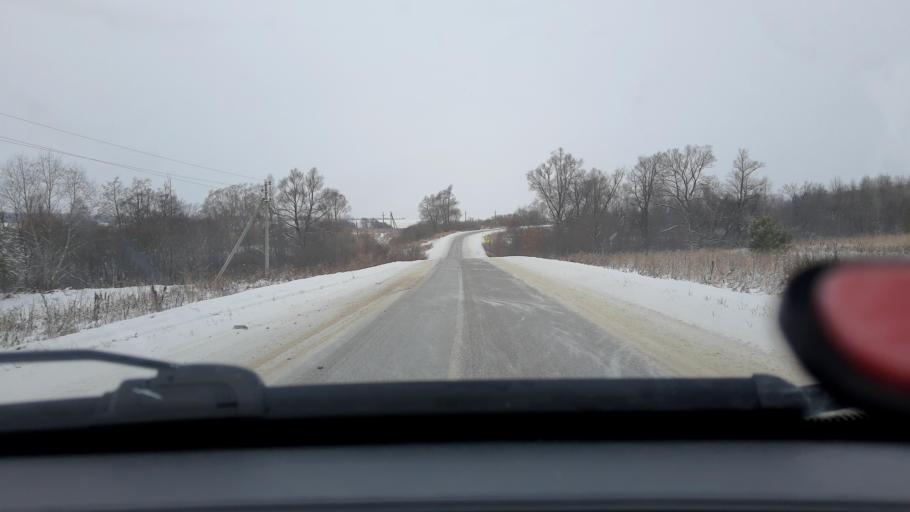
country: RU
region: Bashkortostan
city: Iglino
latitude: 54.6805
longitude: 56.4166
